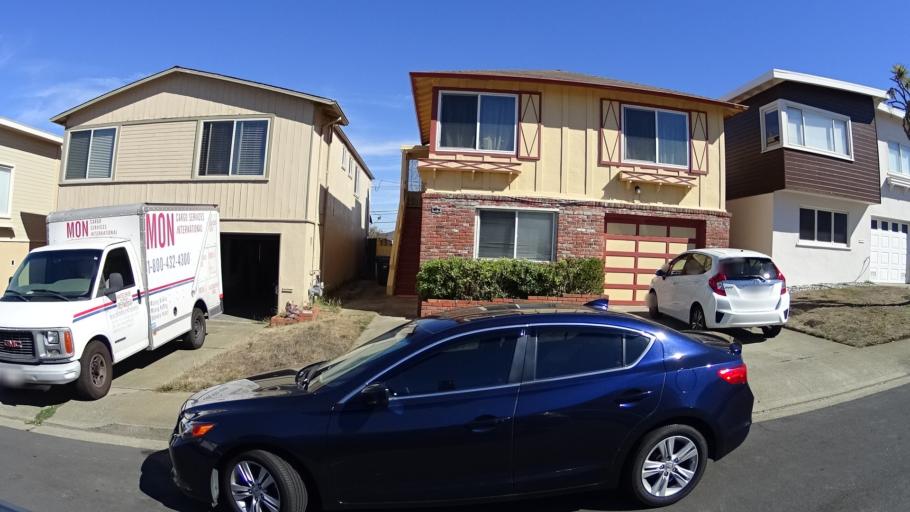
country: US
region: California
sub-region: San Mateo County
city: Broadmoor
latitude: 37.6861
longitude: -122.4907
